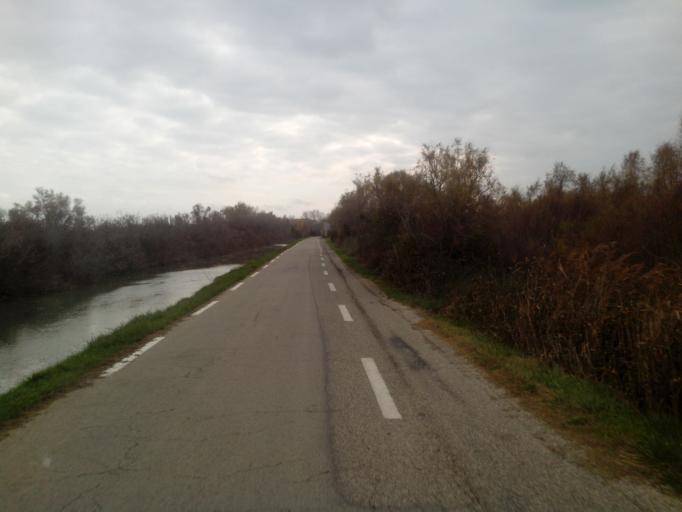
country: FR
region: Languedoc-Roussillon
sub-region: Departement du Gard
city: Vauvert
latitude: 43.6081
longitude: 4.3337
